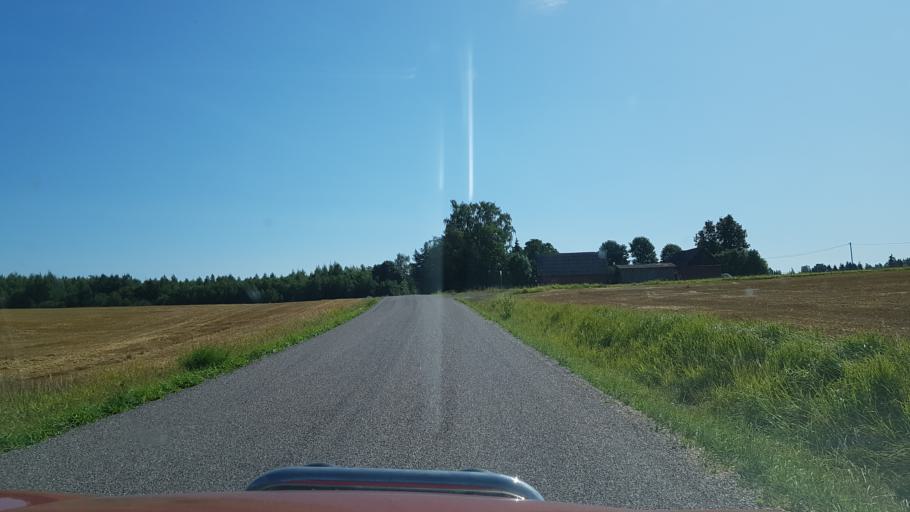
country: EE
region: Tartu
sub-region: Puhja vald
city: Puhja
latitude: 58.2576
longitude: 26.3177
